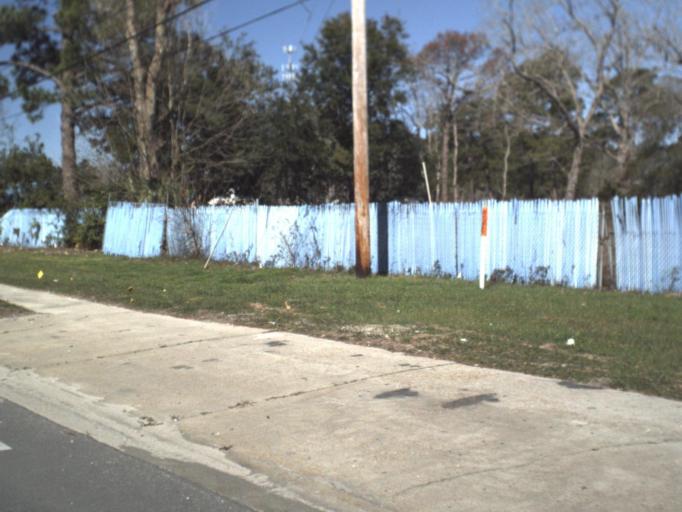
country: US
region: Florida
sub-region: Bay County
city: Callaway
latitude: 30.1529
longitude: -85.5667
